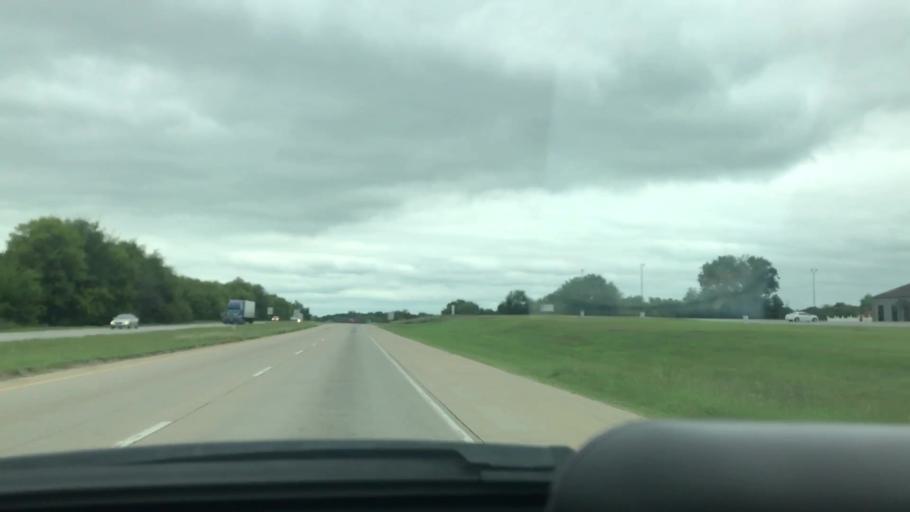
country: US
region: Oklahoma
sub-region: Mayes County
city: Chouteau
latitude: 36.1933
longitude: -95.3418
